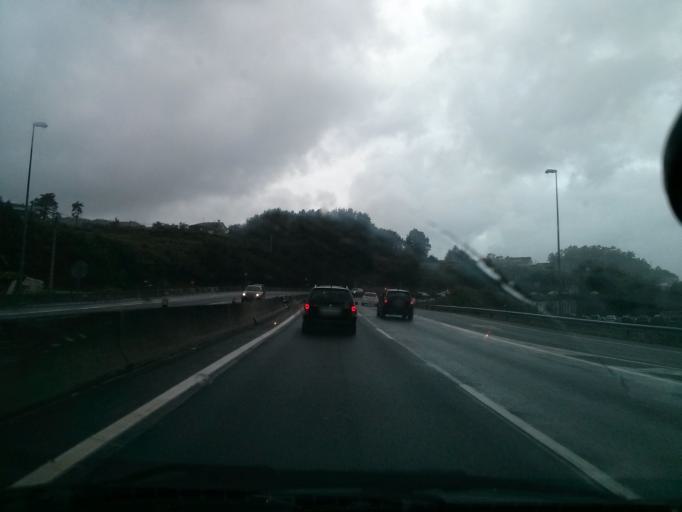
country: ES
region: Galicia
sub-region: Provincia de Pontevedra
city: Porrino
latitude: 42.1837
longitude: -8.6343
